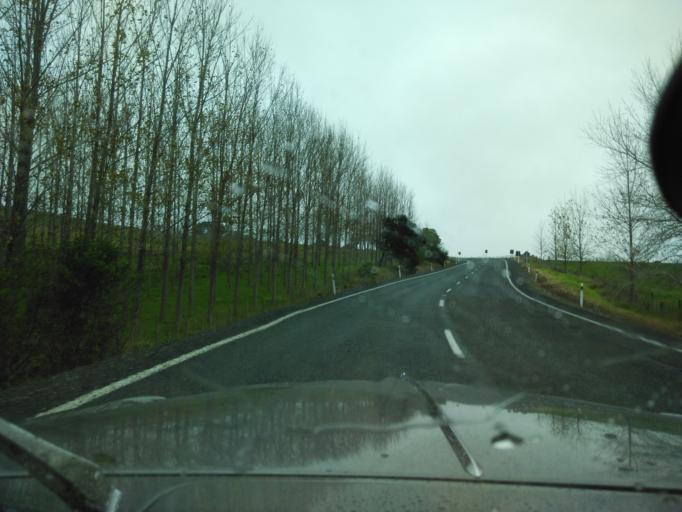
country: NZ
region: Auckland
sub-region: Auckland
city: Wellsford
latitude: -36.3802
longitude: 174.4503
